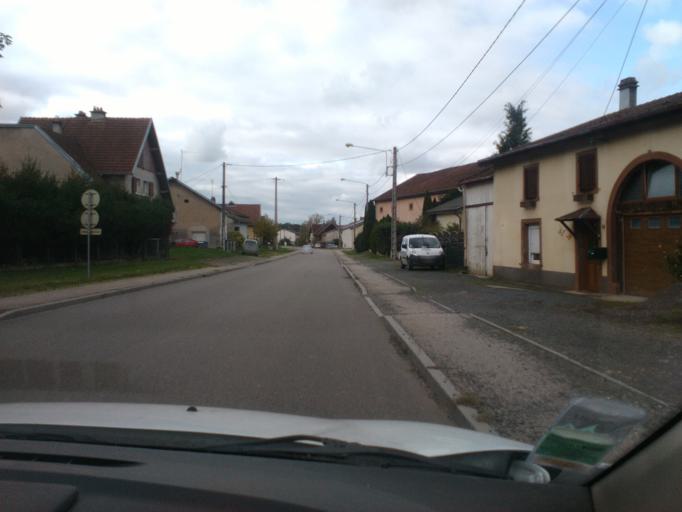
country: FR
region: Lorraine
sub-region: Departement des Vosges
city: Jeanmenil
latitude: 48.3475
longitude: 6.6862
